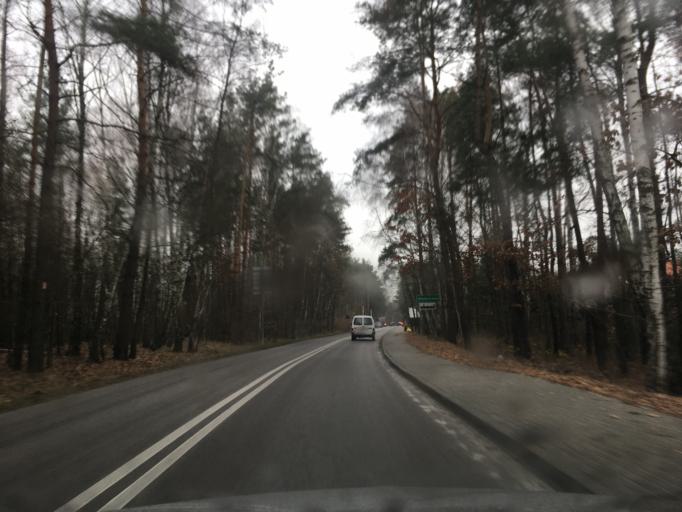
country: PL
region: Masovian Voivodeship
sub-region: Powiat piaseczynski
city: Lesznowola
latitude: 52.0588
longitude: 20.9203
